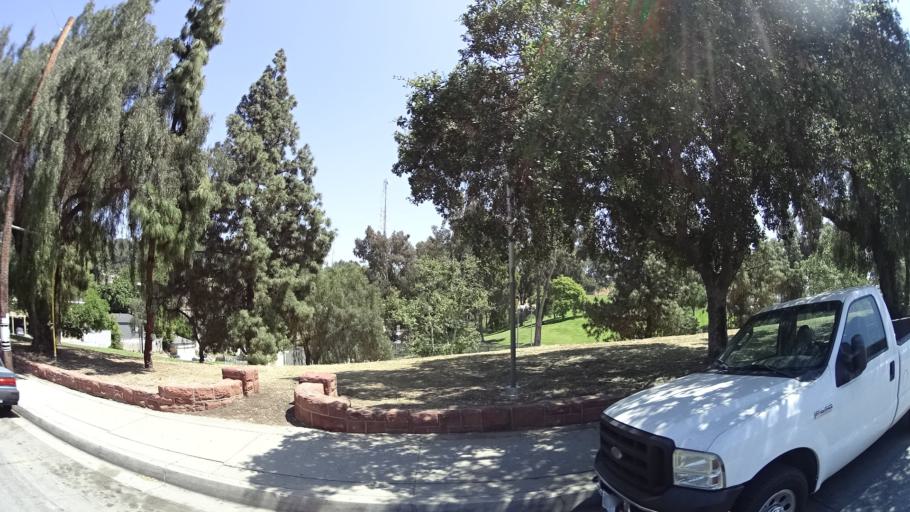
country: US
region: California
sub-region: Los Angeles County
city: Belvedere
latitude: 34.0505
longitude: -118.1789
